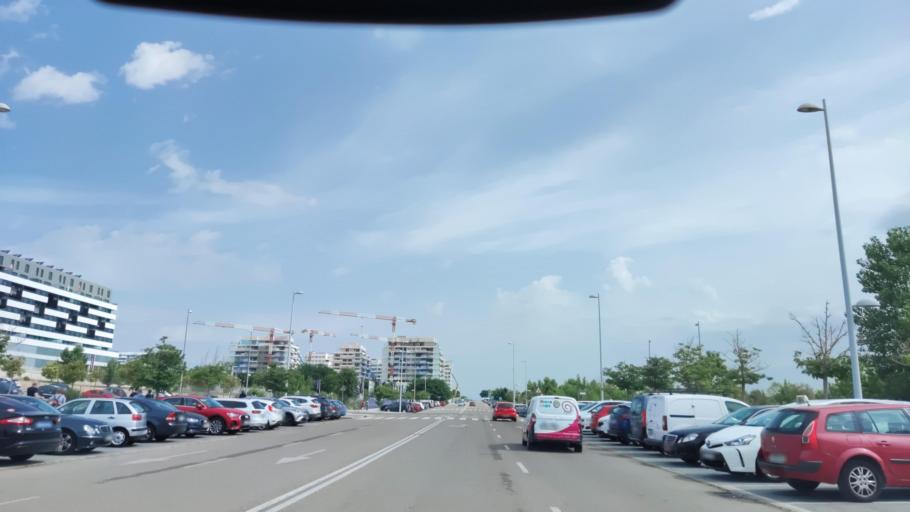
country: ES
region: Madrid
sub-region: Provincia de Madrid
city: Barajas de Madrid
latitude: 40.4869
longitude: -3.6065
